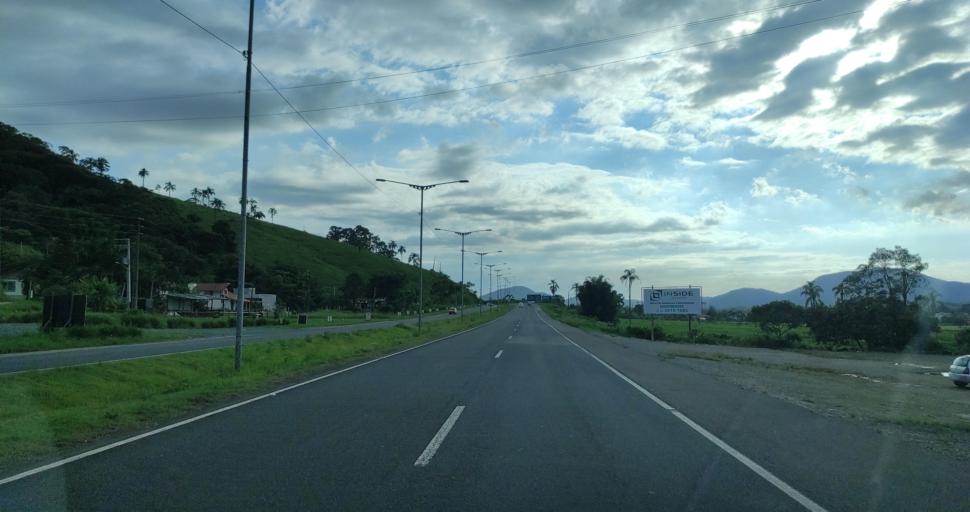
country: BR
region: Santa Catarina
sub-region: Penha
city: Penha
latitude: -26.8091
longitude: -48.6542
